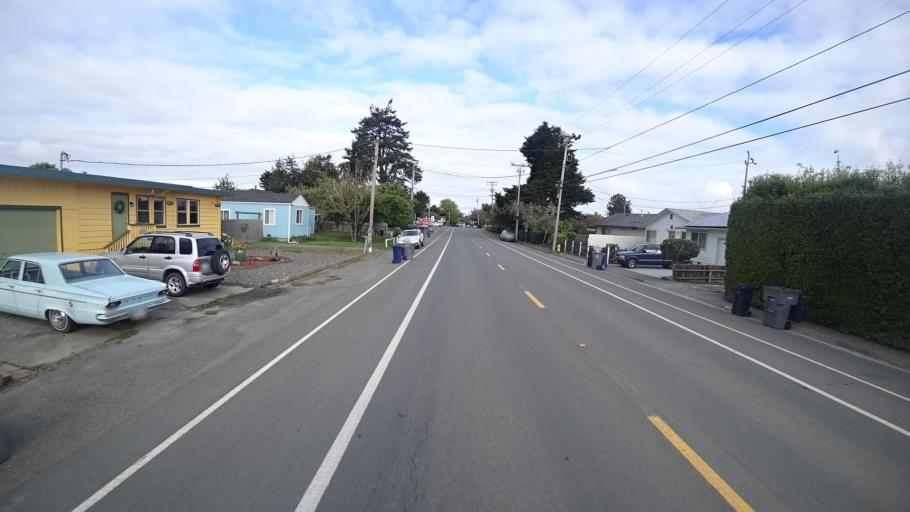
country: US
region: California
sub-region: Humboldt County
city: Arcata
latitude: 40.8898
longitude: -124.0859
